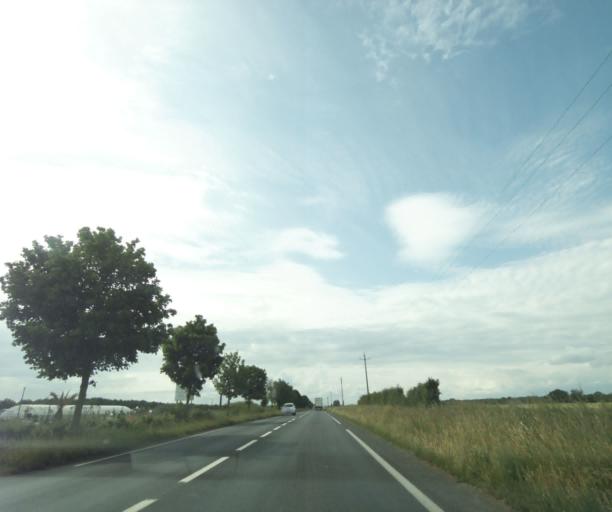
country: FR
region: Pays de la Loire
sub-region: Departement de la Sarthe
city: Solesmes
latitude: 47.8110
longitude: -0.2821
